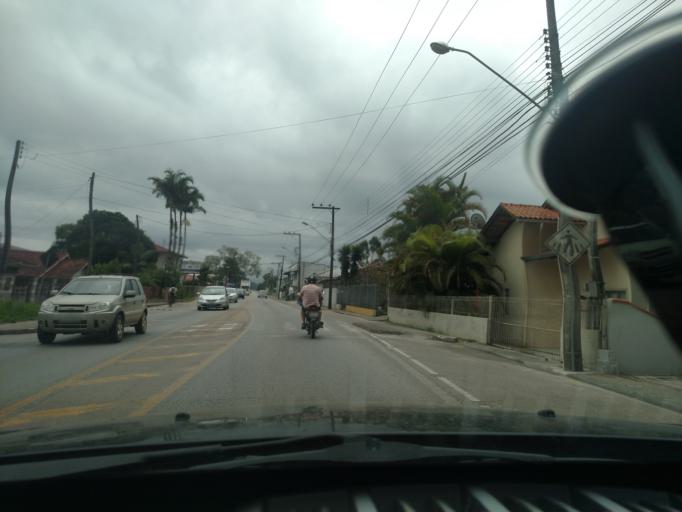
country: BR
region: Santa Catarina
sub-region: Gaspar
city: Gaspar
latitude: -26.9233
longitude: -48.9689
